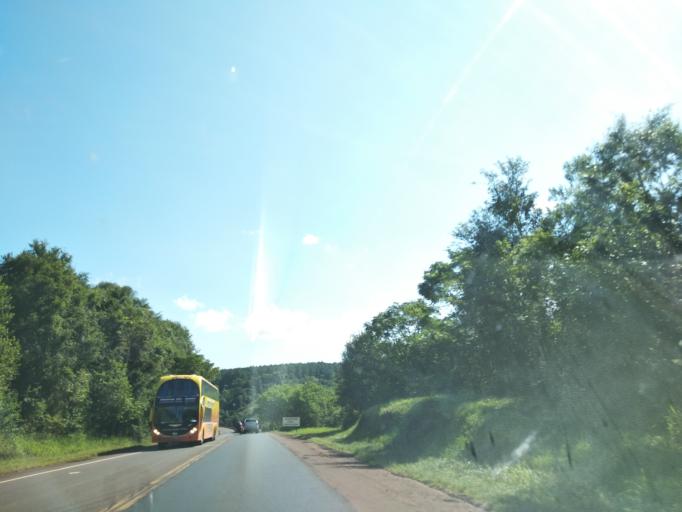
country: AR
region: Misiones
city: Puerto Piray
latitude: -26.4800
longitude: -54.6530
